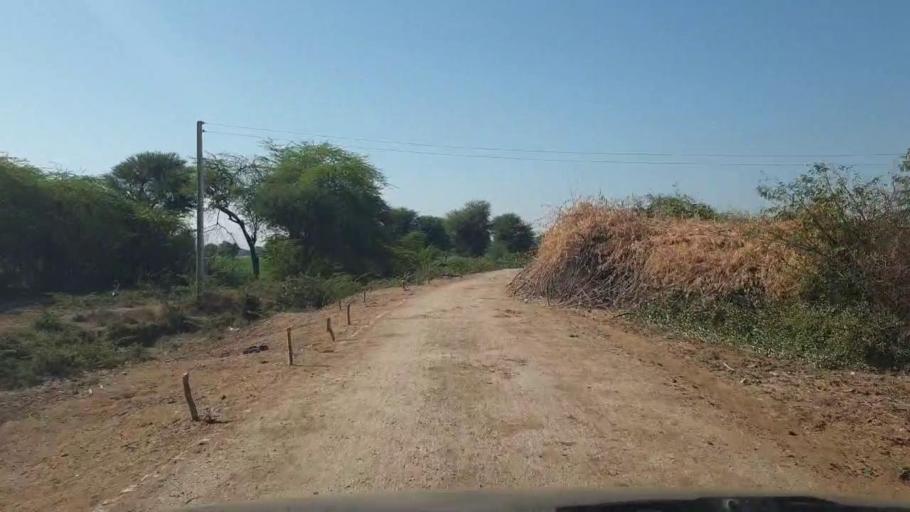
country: PK
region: Sindh
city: Umarkot
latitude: 25.3892
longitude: 69.7029
